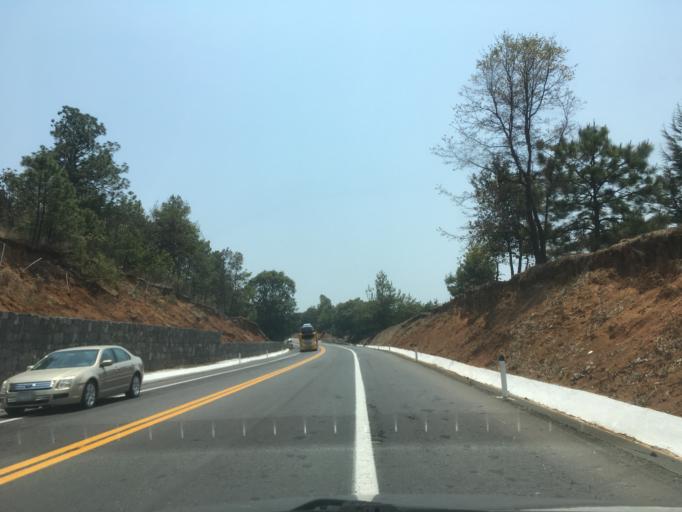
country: MX
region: Michoacan
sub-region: Patzcuaro
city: Santa Ana Chapitiro
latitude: 19.5049
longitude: -101.6868
